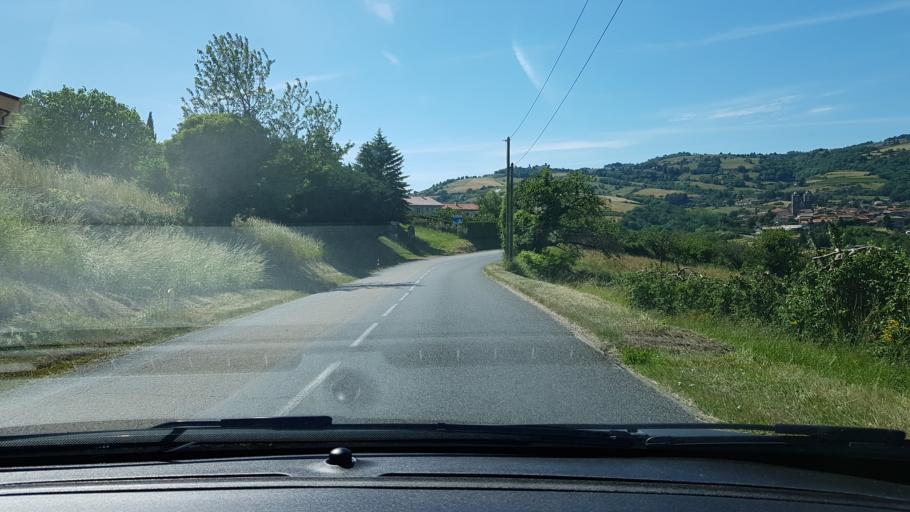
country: FR
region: Rhone-Alpes
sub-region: Departement du Rhone
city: Saint-Didier-sous-Riverie
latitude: 45.5900
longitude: 4.6179
